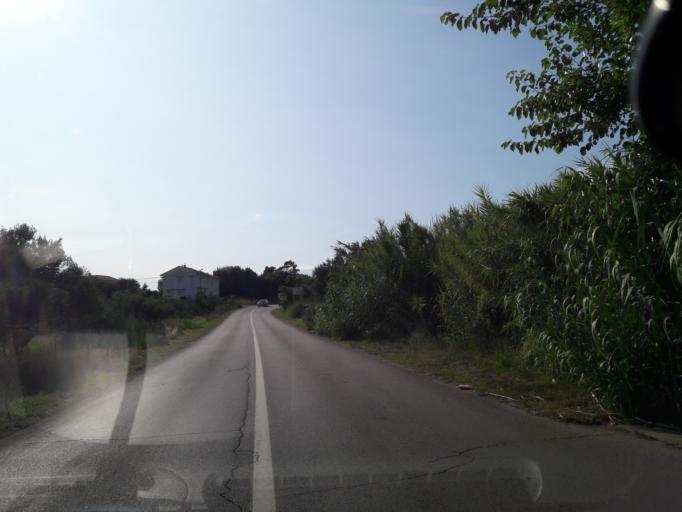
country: HR
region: Primorsko-Goranska
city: Banjol
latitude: 44.7525
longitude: 14.7811
